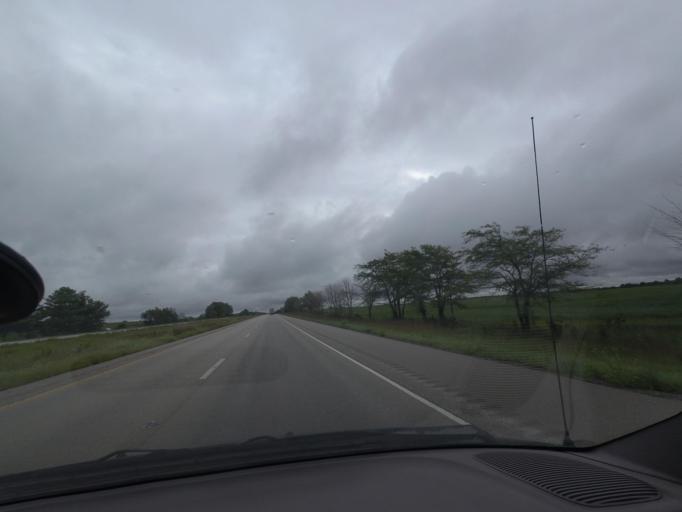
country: US
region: Illinois
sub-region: Macon County
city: Forsyth
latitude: 39.9087
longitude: -88.9386
